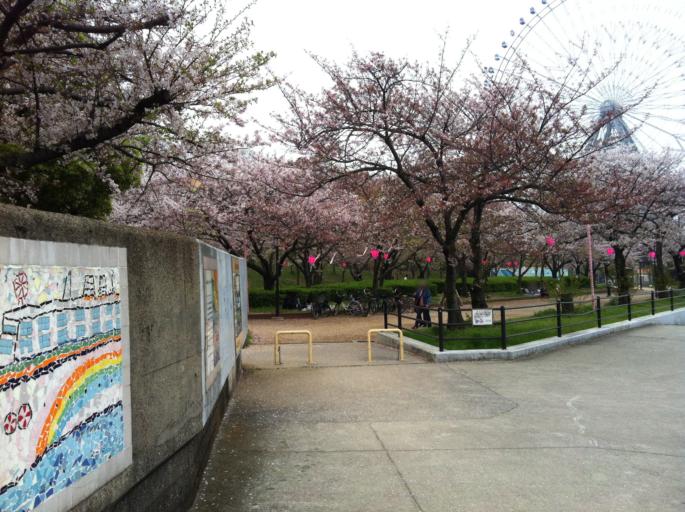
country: JP
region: Hyogo
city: Amagasaki
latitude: 34.6581
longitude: 135.4324
